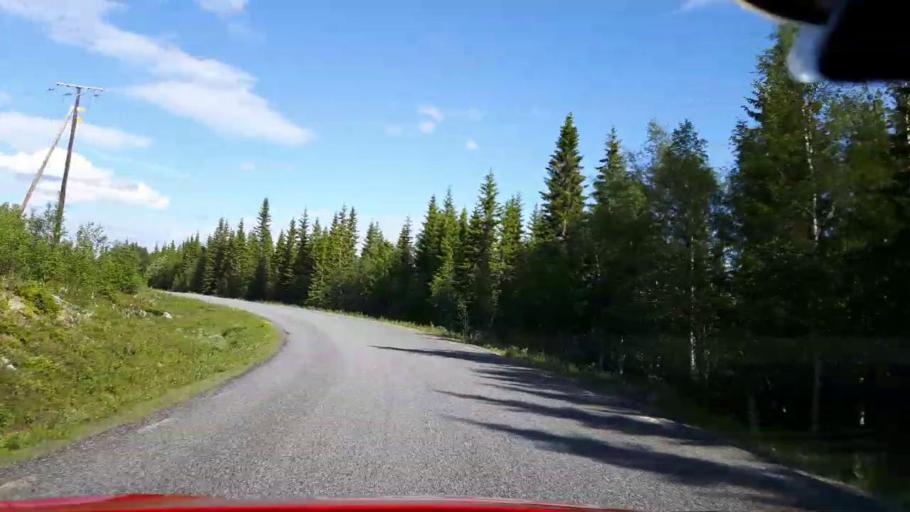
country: SE
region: Jaemtland
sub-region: Krokoms Kommun
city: Valla
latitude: 63.6957
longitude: 14.1838
